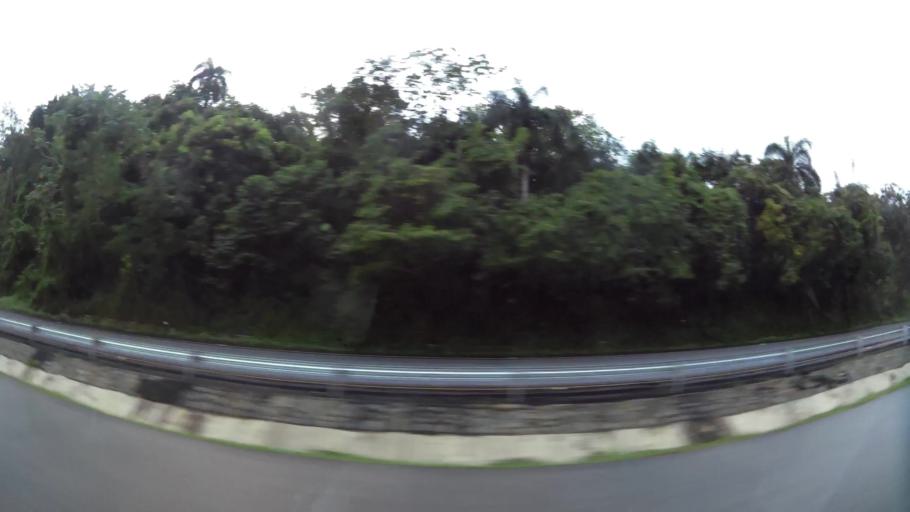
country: DO
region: San Cristobal
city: Villa Altagracia
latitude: 18.5858
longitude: -70.1186
